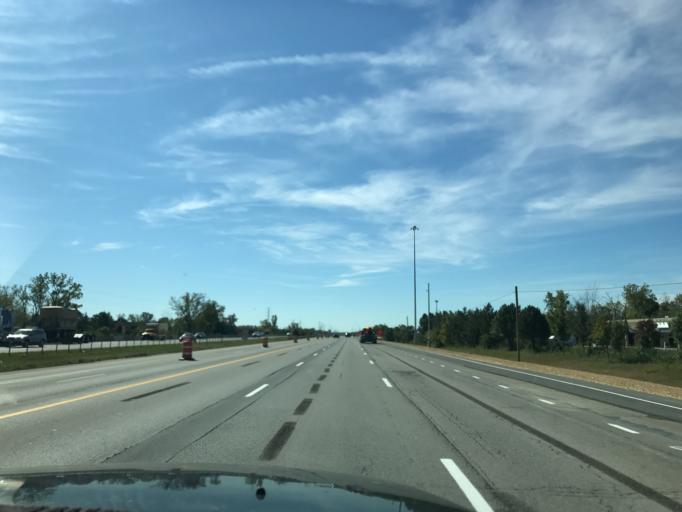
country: US
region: Ohio
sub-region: Franklin County
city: Lincoln Village
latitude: 39.9978
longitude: -83.1186
